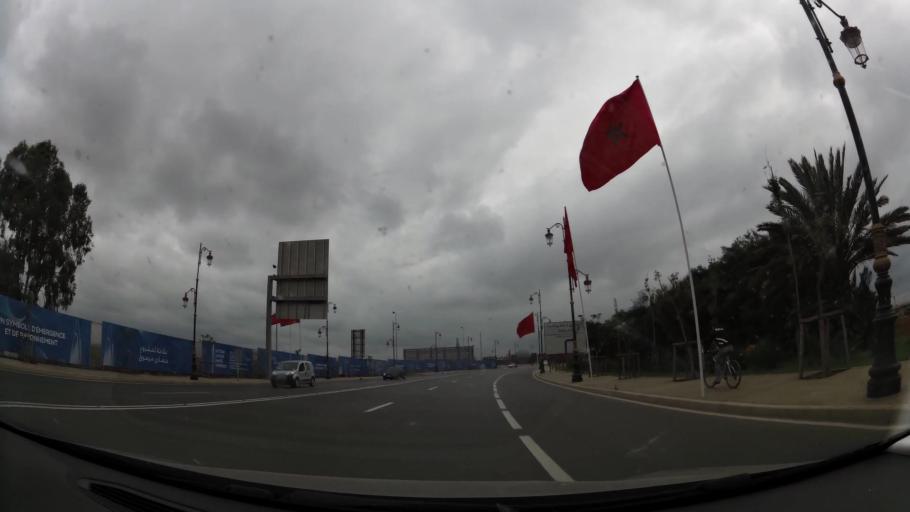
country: MA
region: Rabat-Sale-Zemmour-Zaer
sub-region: Rabat
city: Rabat
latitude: 34.0207
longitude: -6.8054
